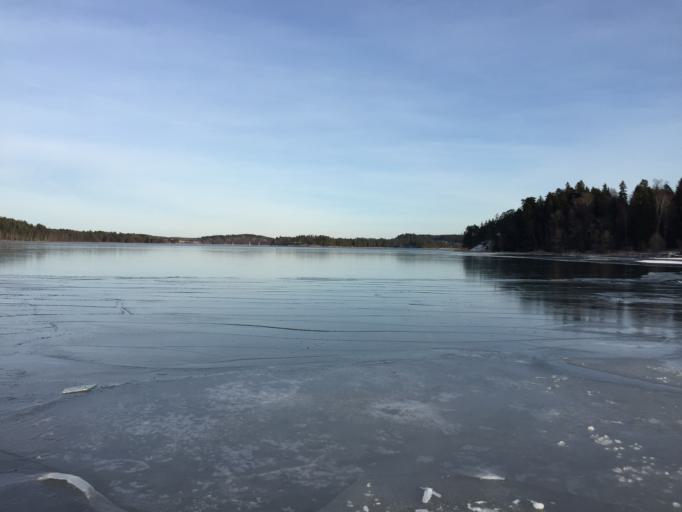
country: SE
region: Stockholm
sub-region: Sodertalje Kommun
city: Pershagen
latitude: 59.0980
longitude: 17.6537
